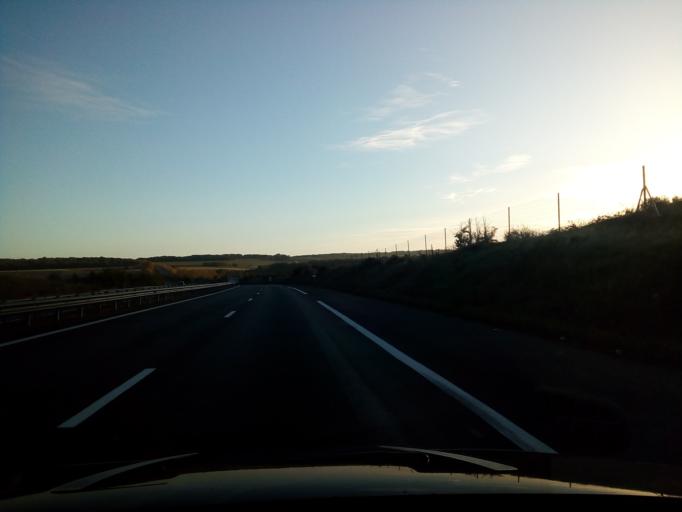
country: FR
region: Poitou-Charentes
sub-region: Departement de la Charente
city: Chateauneuf-sur-Charente
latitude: 45.5459
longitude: -0.0234
